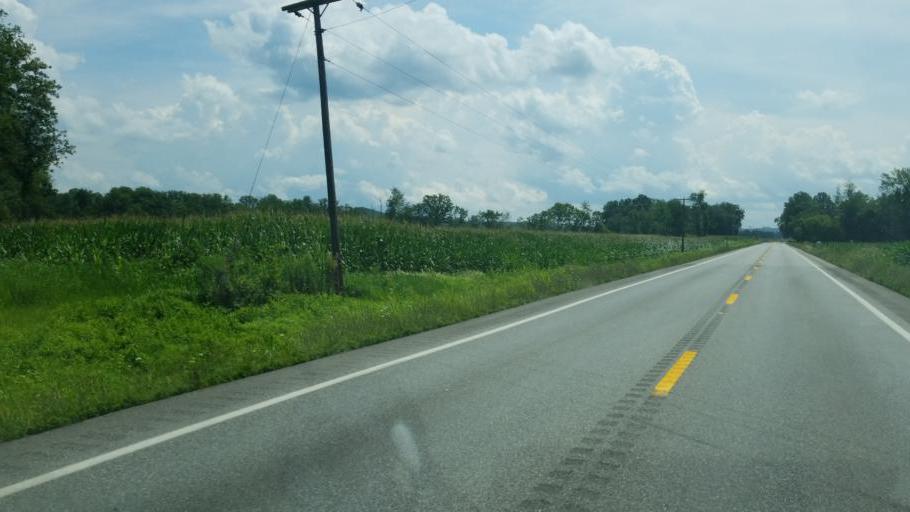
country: US
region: West Virginia
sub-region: Putnam County
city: Buffalo
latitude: 38.6884
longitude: -81.9650
